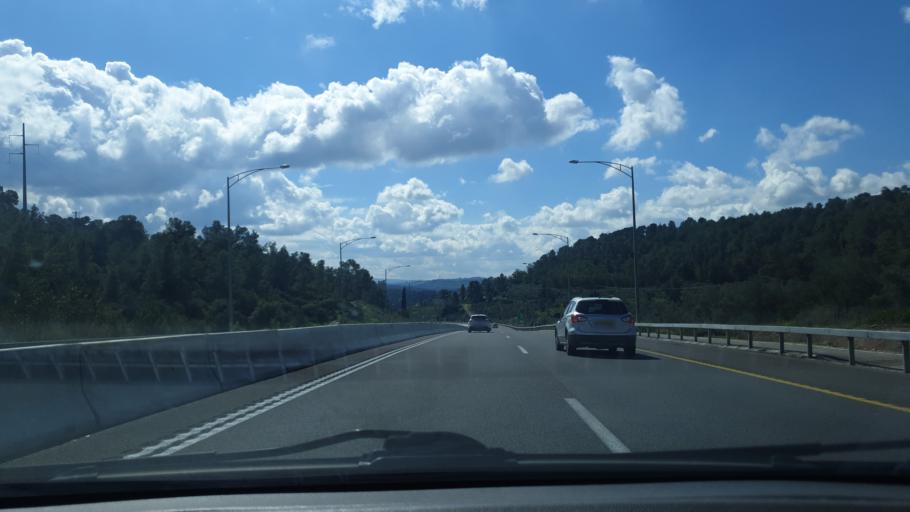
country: IL
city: Mevo horon
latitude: 31.7927
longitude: 35.0144
